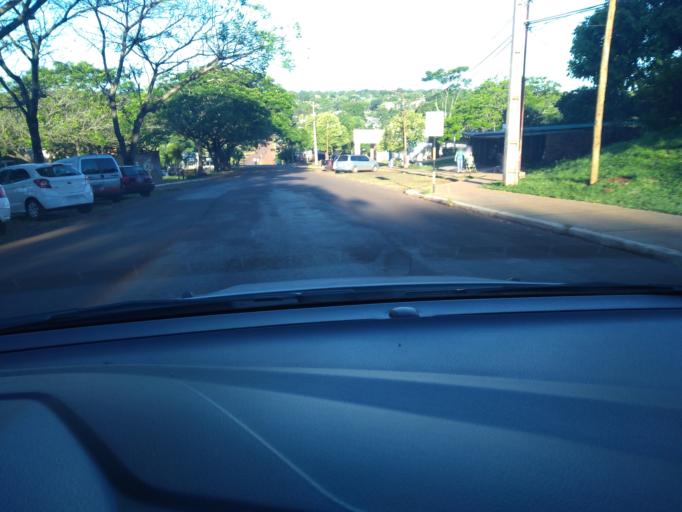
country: AR
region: Misiones
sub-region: Departamento de Obera
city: Obera
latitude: -27.4811
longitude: -55.1099
